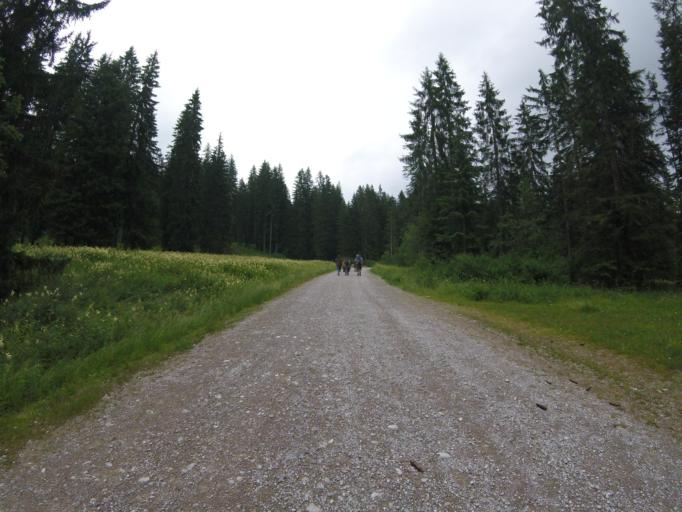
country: AT
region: Tyrol
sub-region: Politischer Bezirk Kitzbuhel
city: Waidring
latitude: 47.6559
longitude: 12.5924
